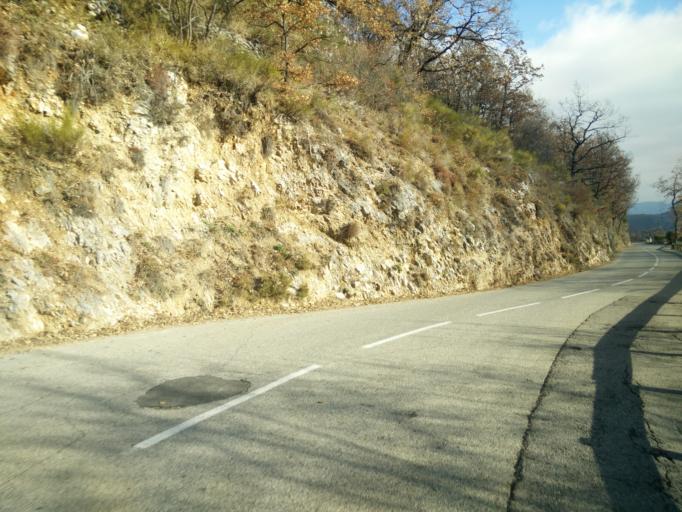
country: FR
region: Provence-Alpes-Cote d'Azur
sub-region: Departement des Alpes-Maritimes
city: Le Broc
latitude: 43.8147
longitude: 7.1047
